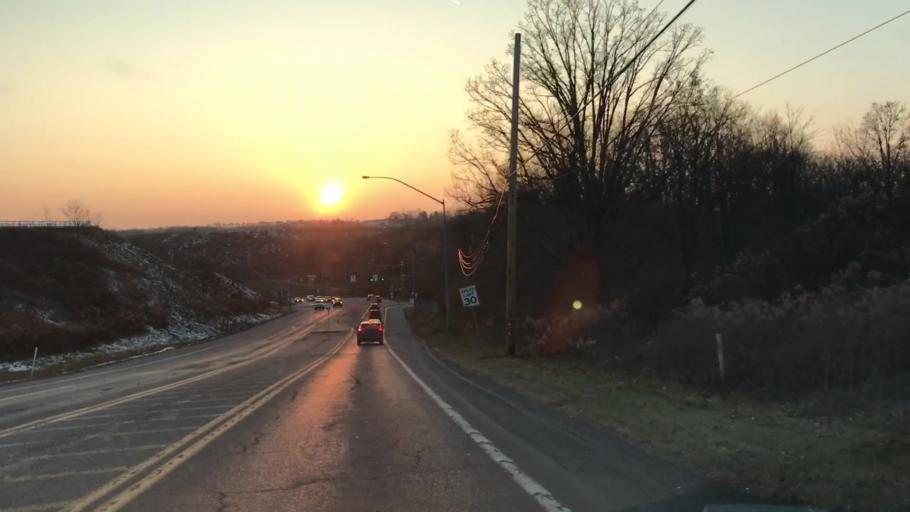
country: US
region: Pennsylvania
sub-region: Allegheny County
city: Carnot-Moon
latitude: 40.4838
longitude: -80.1980
